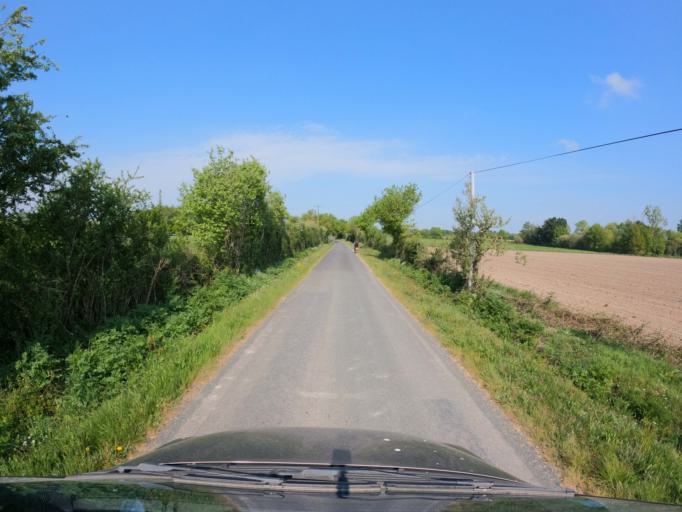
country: FR
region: Pays de la Loire
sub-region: Departement de la Vendee
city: Treize-Septiers
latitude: 46.9994
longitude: -1.2313
